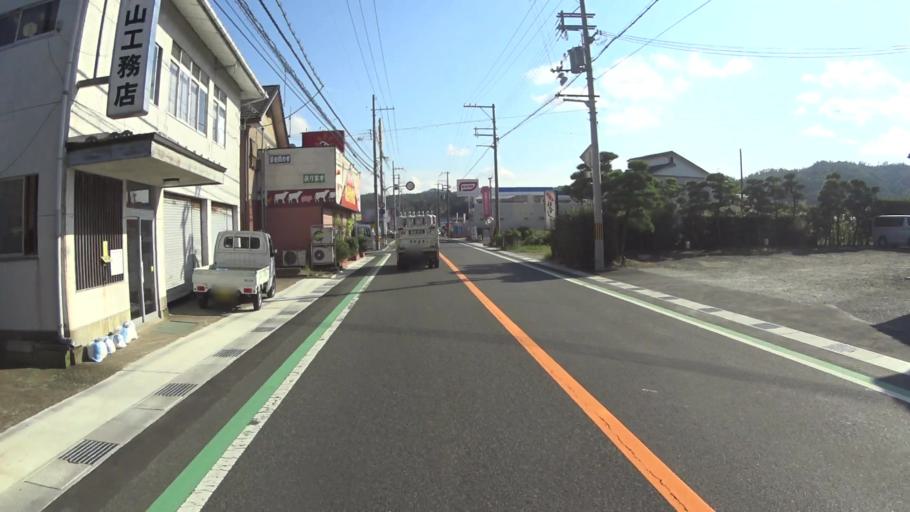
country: JP
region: Kyoto
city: Miyazu
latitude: 35.6733
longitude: 135.0280
